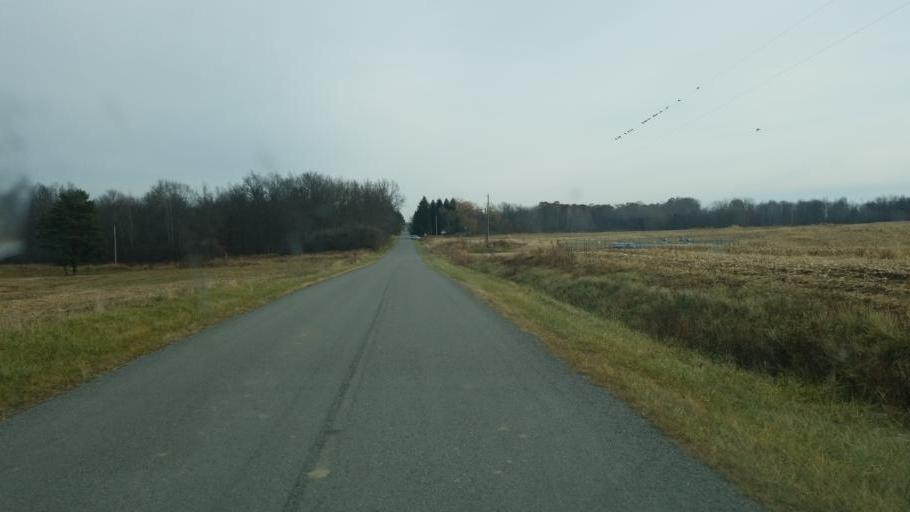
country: US
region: Pennsylvania
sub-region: Crawford County
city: Cochranton
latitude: 41.5021
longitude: -80.1056
